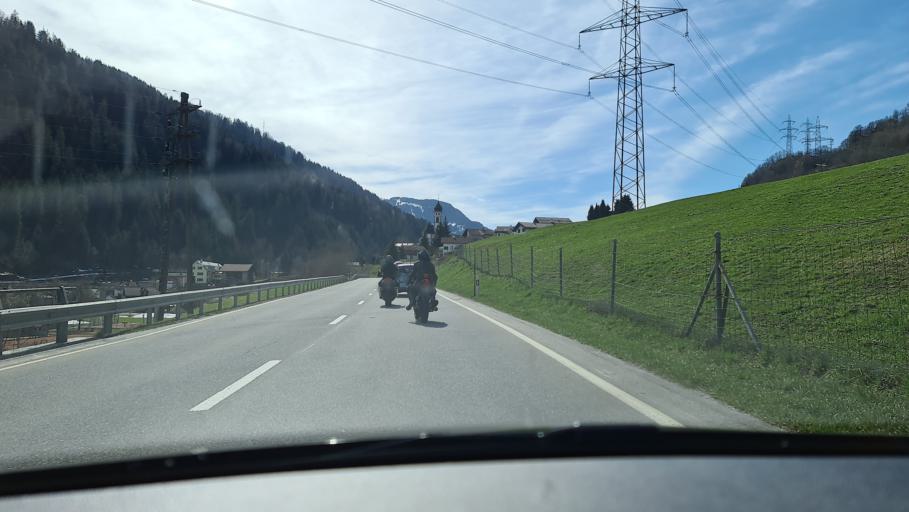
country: CH
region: Grisons
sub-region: Surselva District
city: Breil
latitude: 46.7567
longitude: 9.0614
